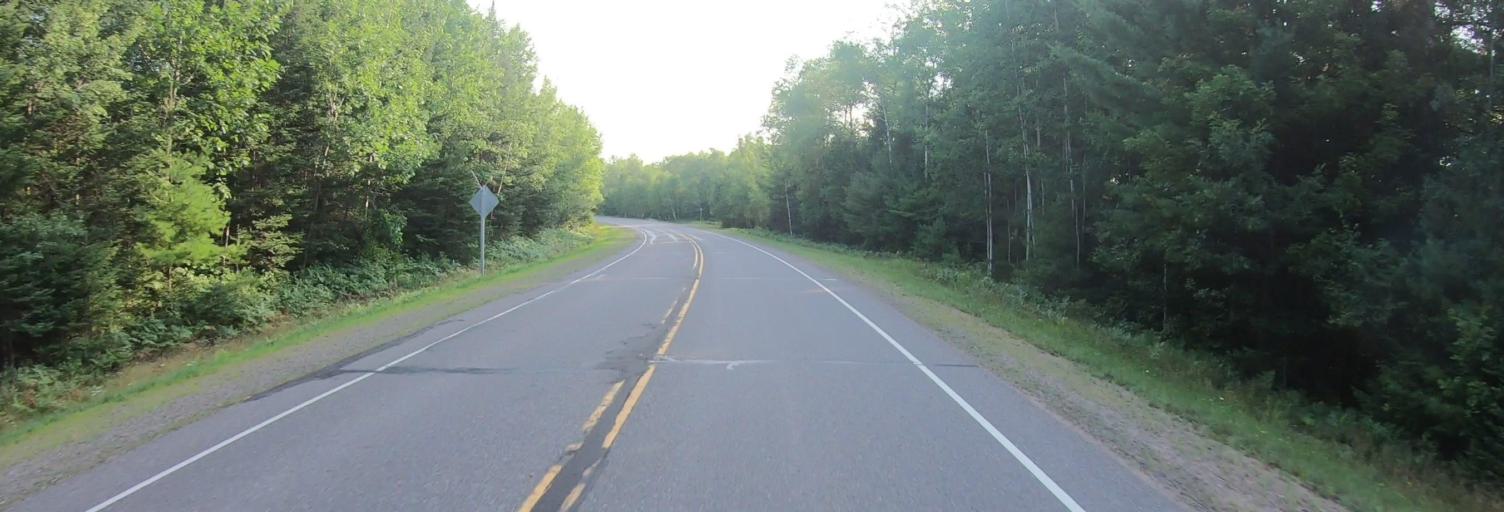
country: US
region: Wisconsin
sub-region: Ashland County
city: Ashland
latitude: 46.1637
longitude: -90.9129
